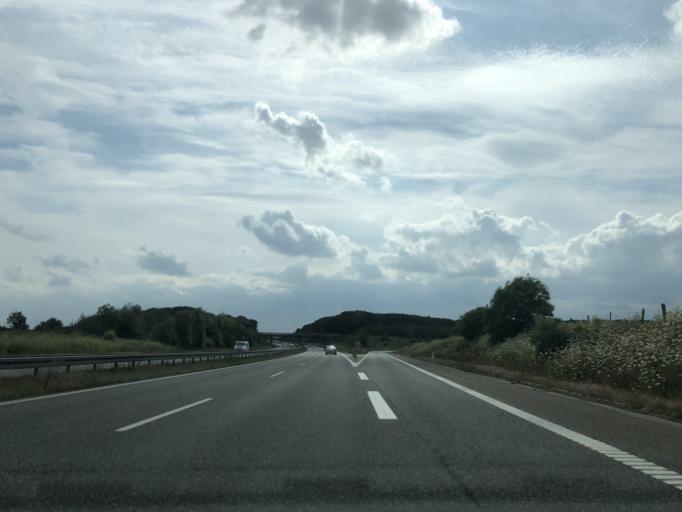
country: DK
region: Central Jutland
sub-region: Skanderborg Kommune
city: Skovby
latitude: 56.1501
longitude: 9.9739
